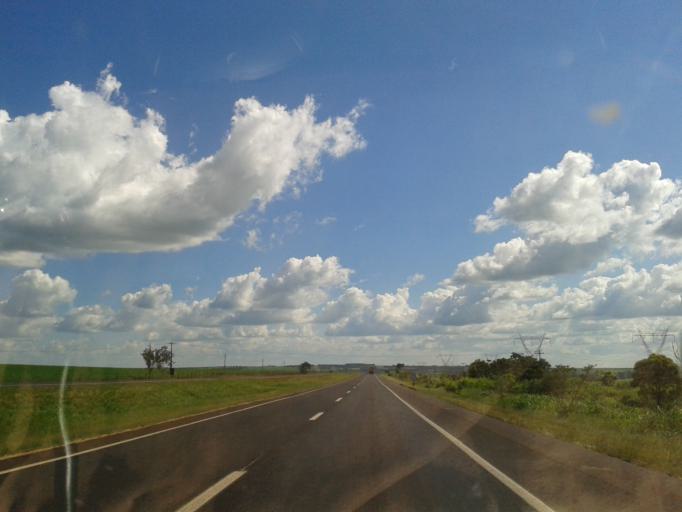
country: BR
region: Goias
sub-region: Goiatuba
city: Goiatuba
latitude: -17.9749
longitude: -49.2555
